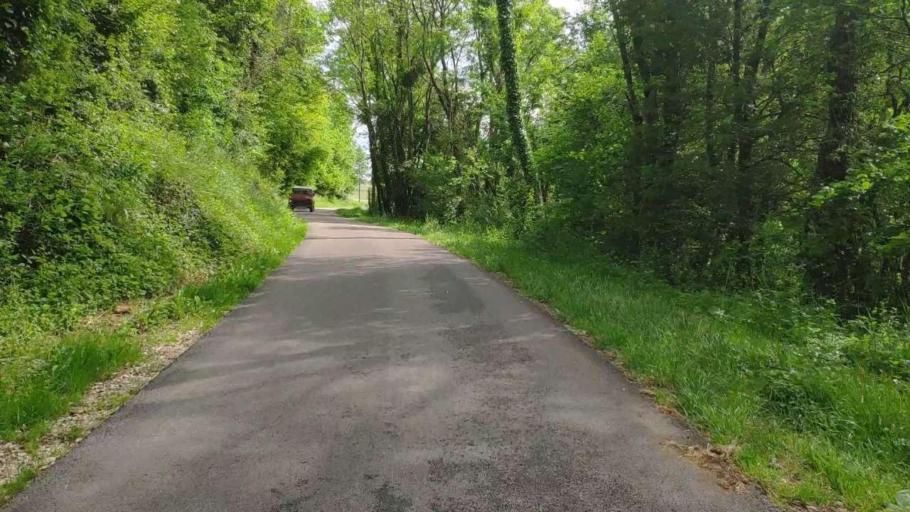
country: FR
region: Franche-Comte
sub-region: Departement du Jura
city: Poligny
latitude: 46.7743
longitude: 5.6268
